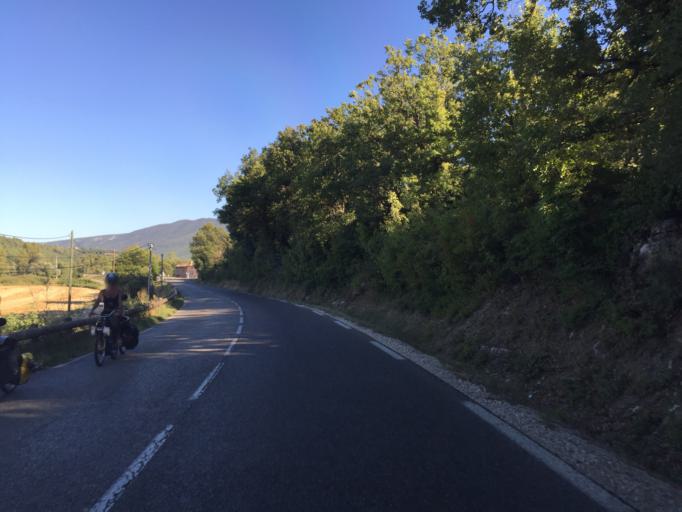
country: FR
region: Provence-Alpes-Cote d'Azur
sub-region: Departement du Vaucluse
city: Saignon
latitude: 43.8683
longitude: 5.4556
